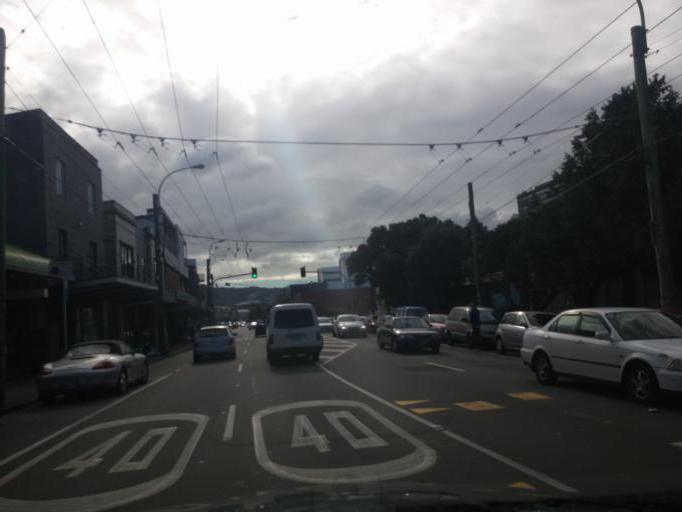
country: NZ
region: Wellington
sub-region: Wellington City
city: Wellington
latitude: -41.3117
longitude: 174.7791
